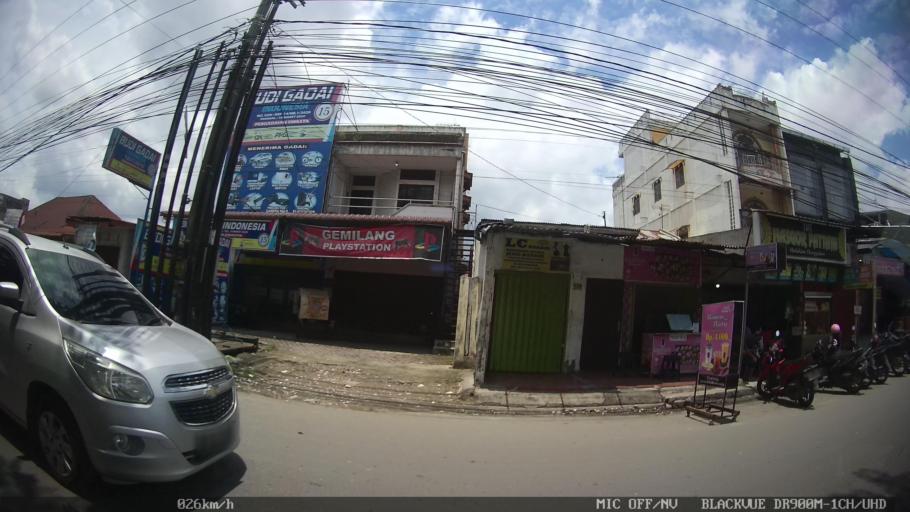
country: ID
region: North Sumatra
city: Medan
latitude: 3.6062
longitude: 98.7063
